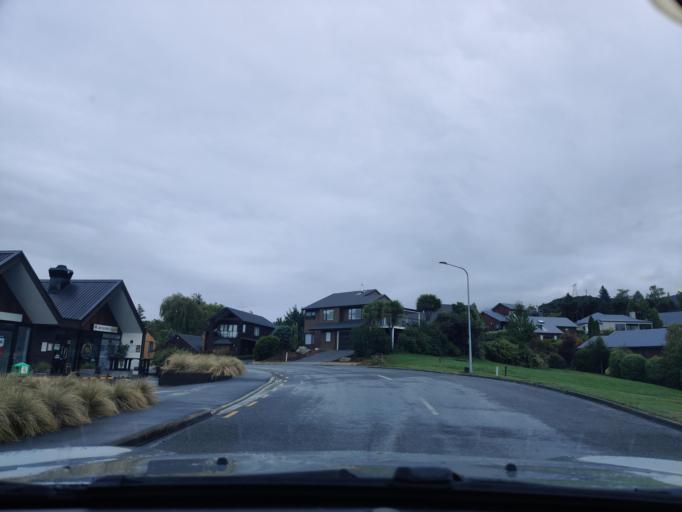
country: NZ
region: Canterbury
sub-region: Hurunui District
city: Amberley
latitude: -42.5199
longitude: 172.8274
